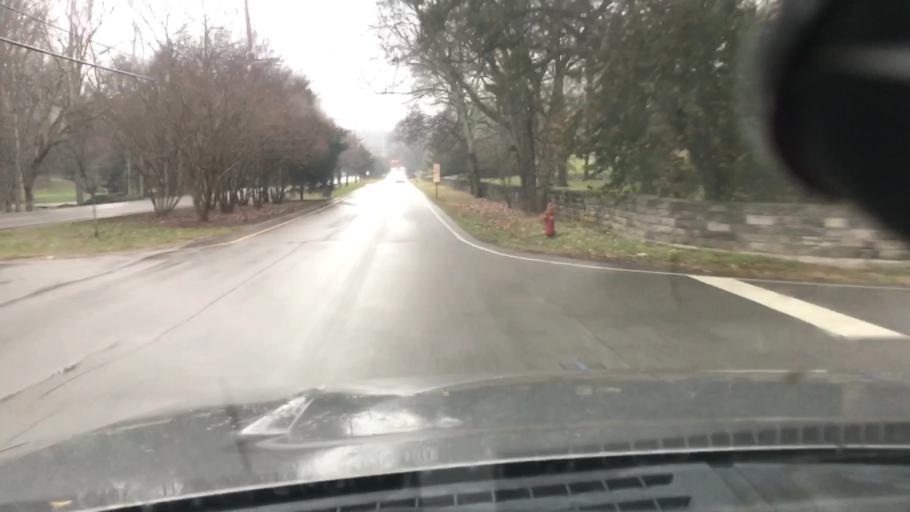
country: US
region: Tennessee
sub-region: Davidson County
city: Belle Meade
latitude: 36.1140
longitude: -86.8545
